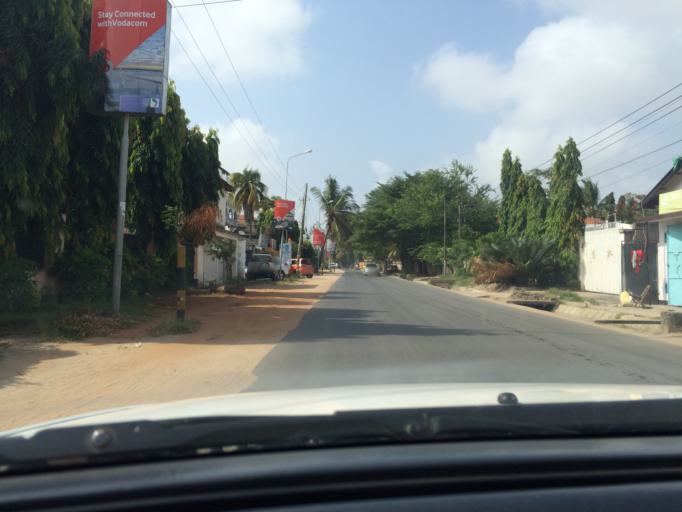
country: TZ
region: Dar es Salaam
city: Magomeni
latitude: -6.7590
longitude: 39.2719
